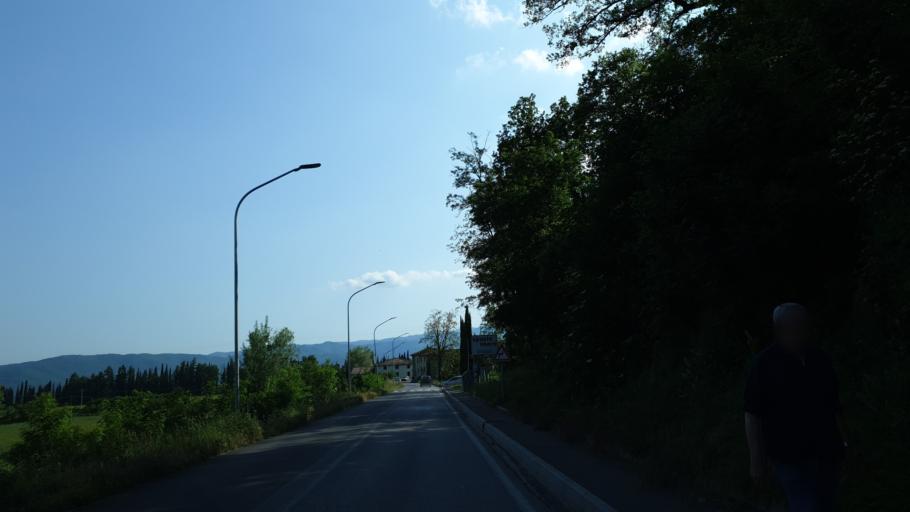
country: IT
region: Tuscany
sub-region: Province of Arezzo
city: Soci
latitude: 43.7475
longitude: 11.8198
